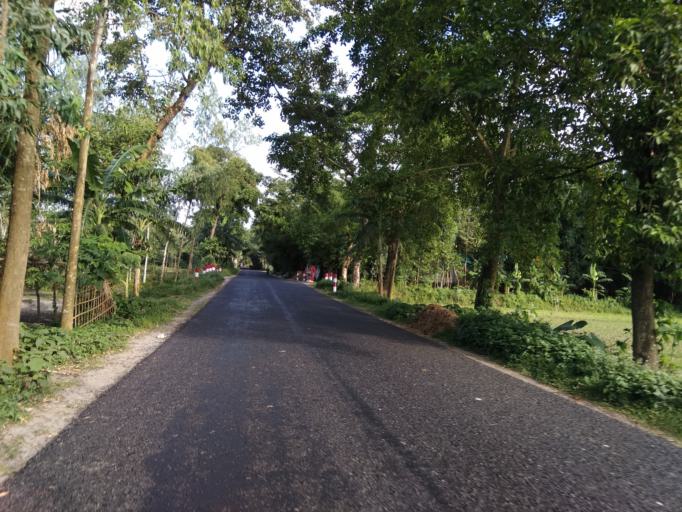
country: BD
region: Rangpur Division
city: Rangpur
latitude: 25.8335
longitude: 89.1167
